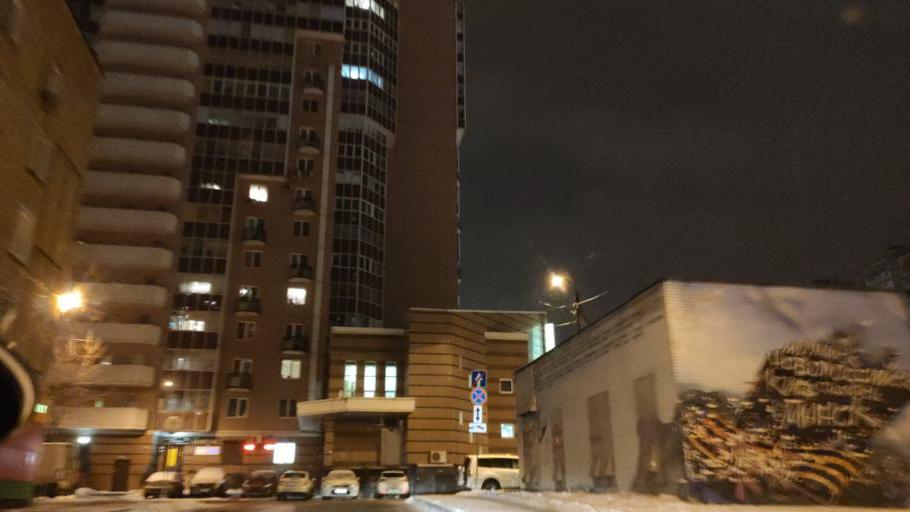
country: RU
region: Moskovskaya
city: Odintsovo
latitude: 55.6855
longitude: 37.3045
